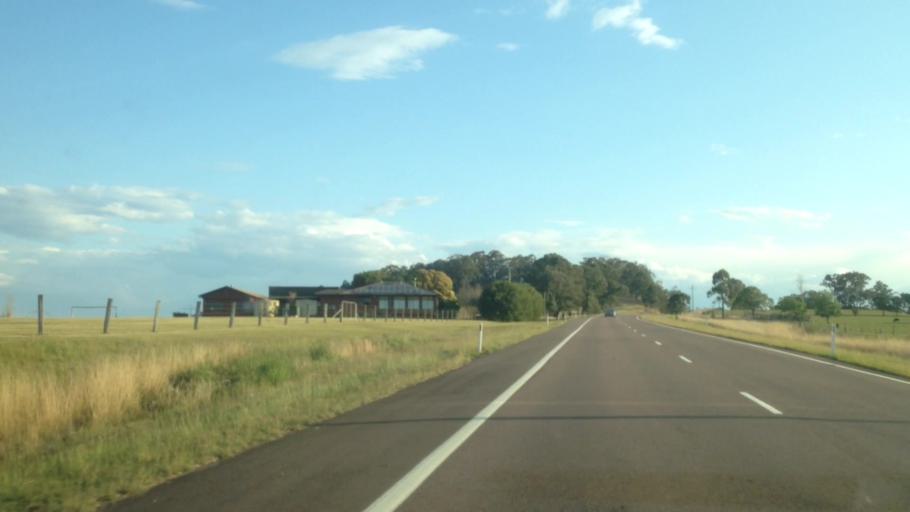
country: AU
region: New South Wales
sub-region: Cessnock
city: Kurri Kurri
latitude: -32.8791
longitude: 151.4740
